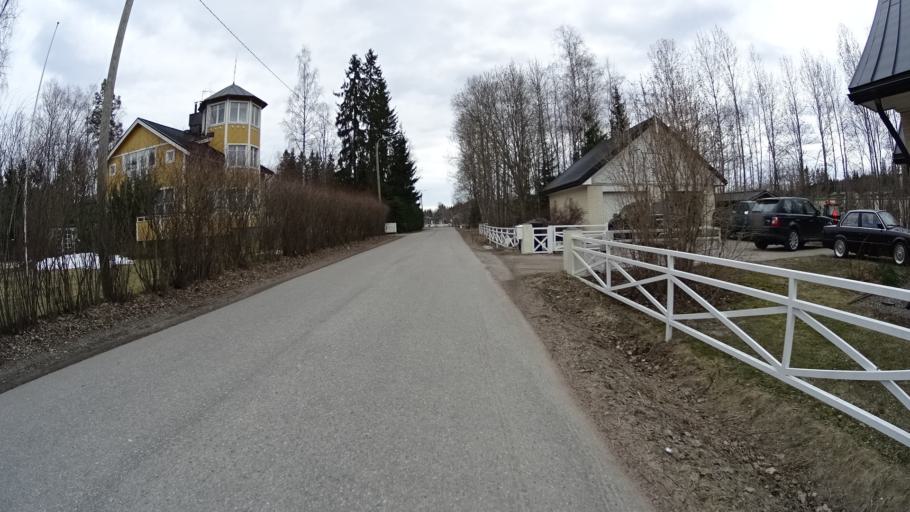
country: FI
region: Uusimaa
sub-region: Helsinki
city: Kilo
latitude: 60.2893
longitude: 24.7857
